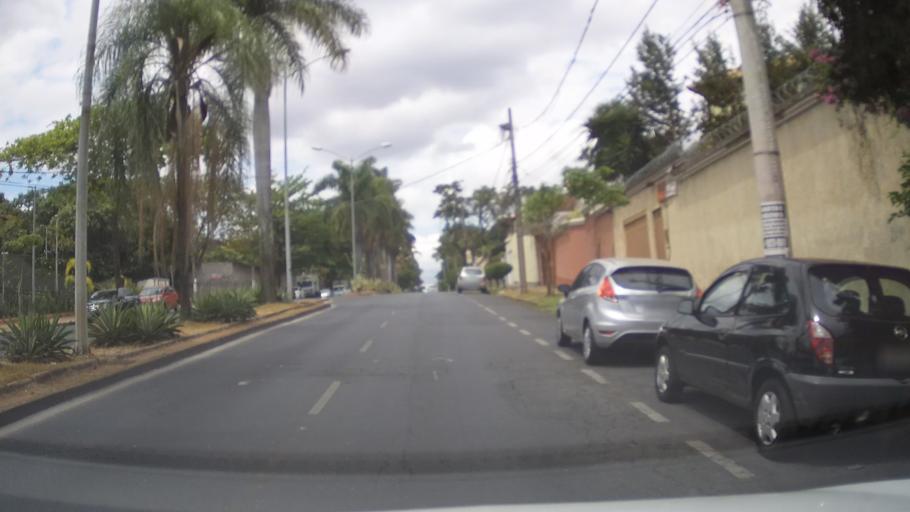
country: BR
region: Minas Gerais
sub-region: Belo Horizonte
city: Belo Horizonte
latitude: -19.8539
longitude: -43.9666
